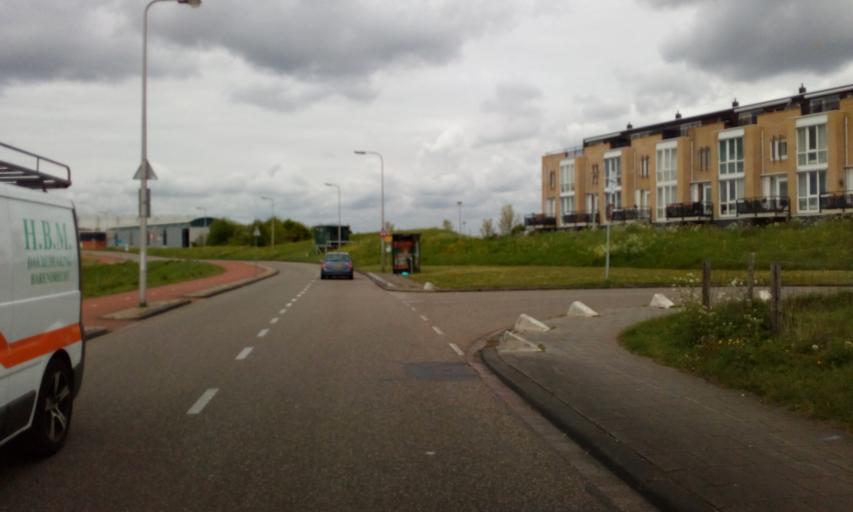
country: NL
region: South Holland
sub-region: Gemeente Capelle aan den IJssel
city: Capelle-West
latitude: 51.8982
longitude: 4.5818
